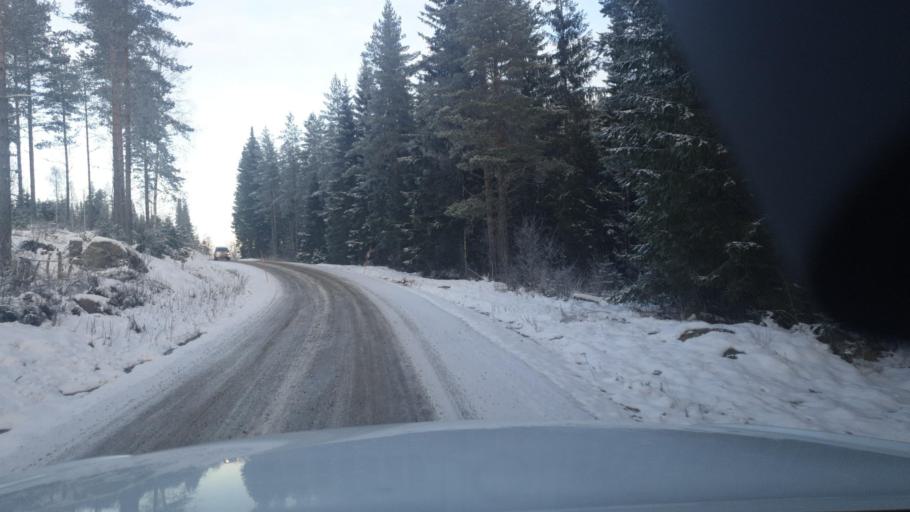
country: SE
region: Vaermland
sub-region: Arvika Kommun
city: Arvika
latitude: 59.9860
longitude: 12.6612
